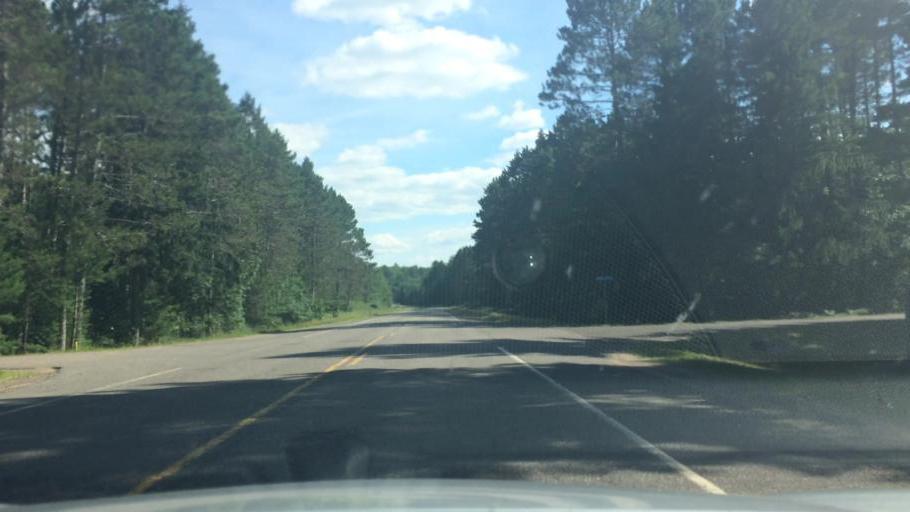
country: US
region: Wisconsin
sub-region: Vilas County
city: Lac du Flambeau
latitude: 46.0510
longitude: -89.6500
